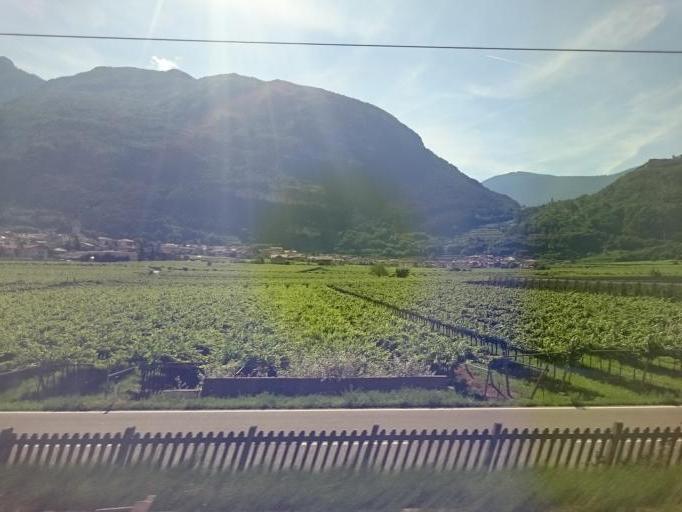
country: IT
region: Trentino-Alto Adige
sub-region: Provincia di Trento
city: Besenello
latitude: 45.9421
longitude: 11.1005
